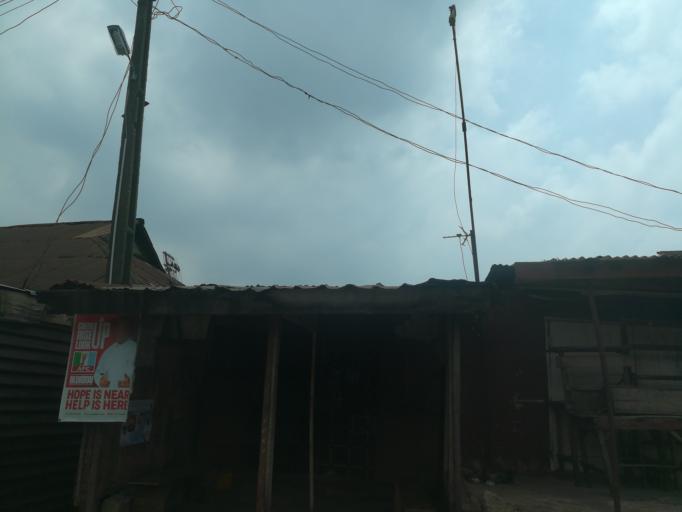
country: NG
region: Lagos
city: Ikorodu
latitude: 6.6135
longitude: 3.5126
